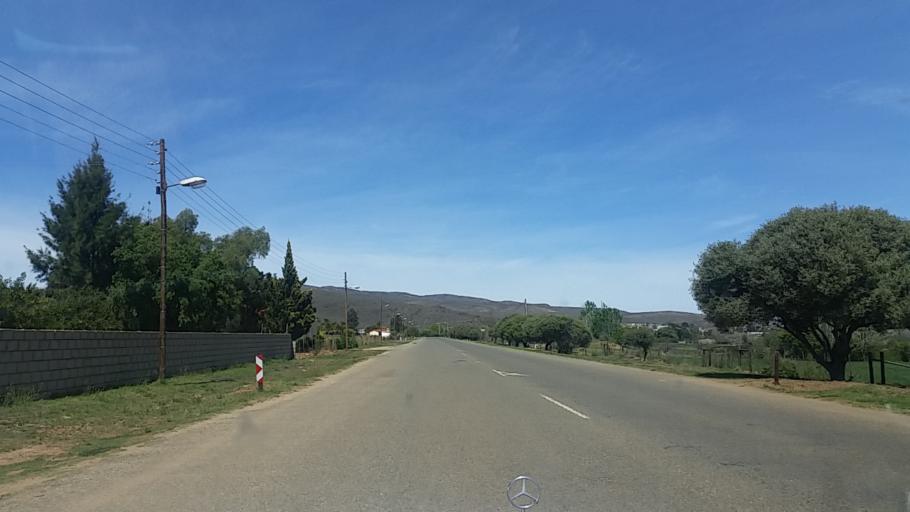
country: ZA
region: Western Cape
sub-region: Eden District Municipality
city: Knysna
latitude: -33.6458
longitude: 23.1367
